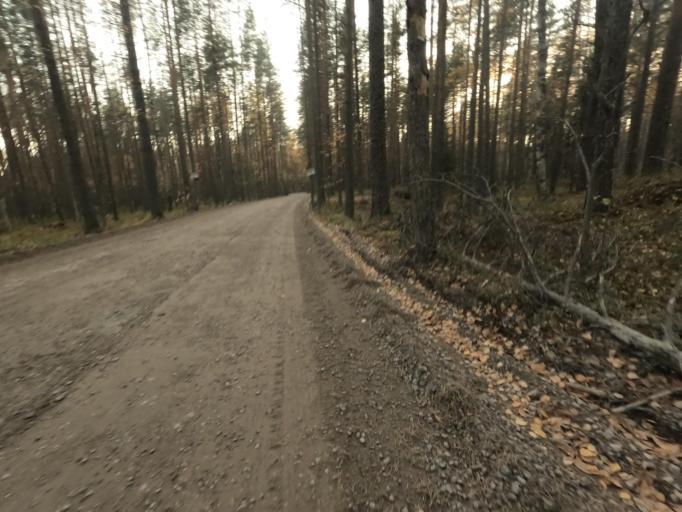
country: RU
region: St.-Petersburg
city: Repino
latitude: 60.1861
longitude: 29.8685
